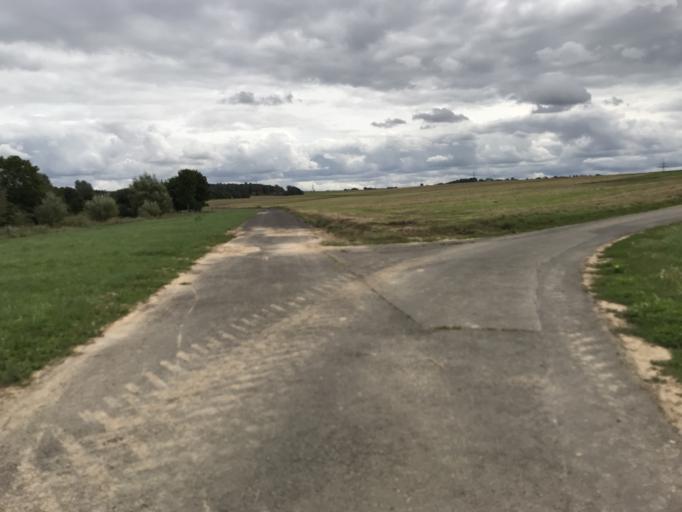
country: DE
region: Hesse
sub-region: Regierungsbezirk Giessen
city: Grunberg
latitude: 50.6319
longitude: 8.9498
